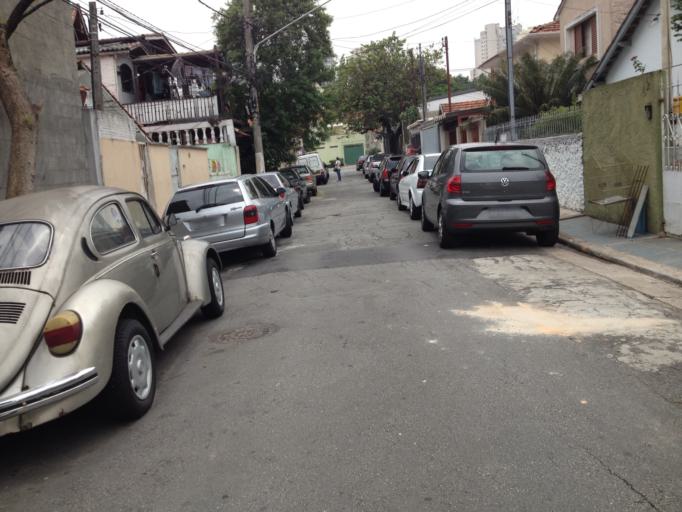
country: BR
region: Sao Paulo
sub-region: Sao Paulo
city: Sao Paulo
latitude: -23.5976
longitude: -46.6769
